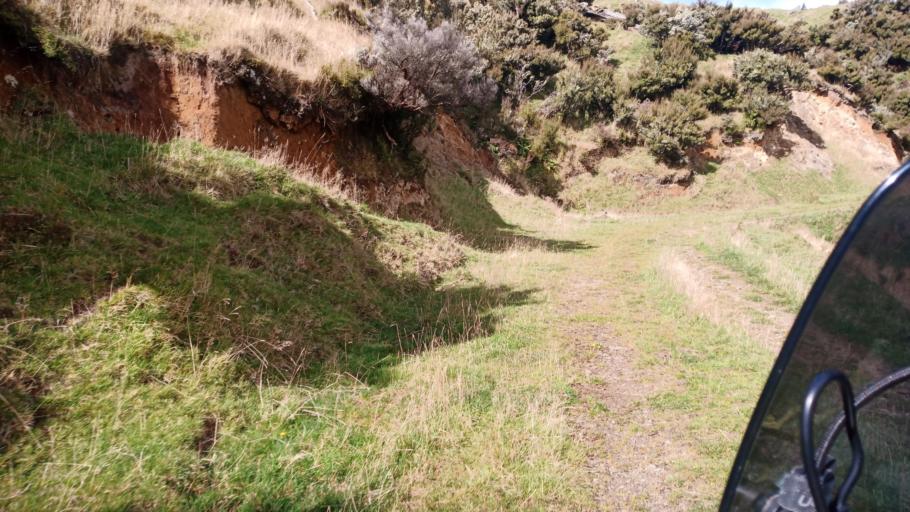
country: NZ
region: Gisborne
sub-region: Gisborne District
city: Gisborne
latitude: -38.4737
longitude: 177.5347
